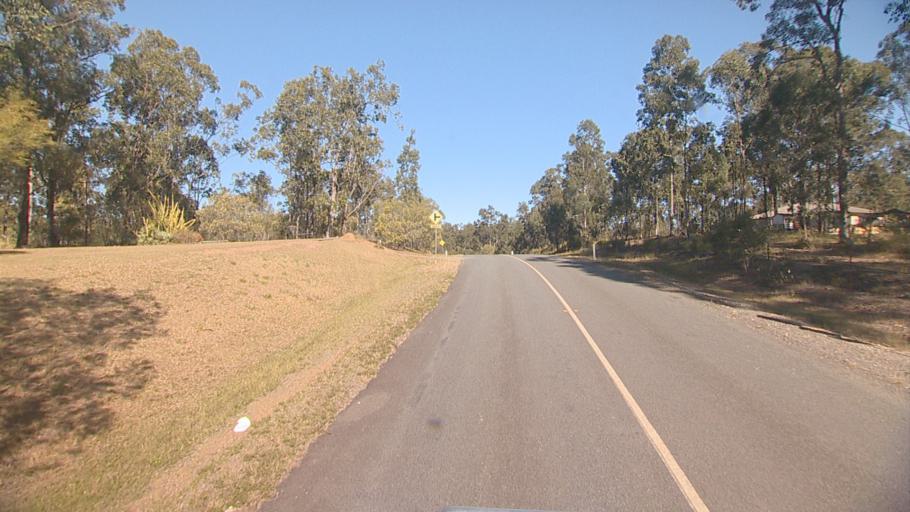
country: AU
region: Queensland
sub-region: Ipswich
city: Springfield Lakes
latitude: -27.7130
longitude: 152.9180
